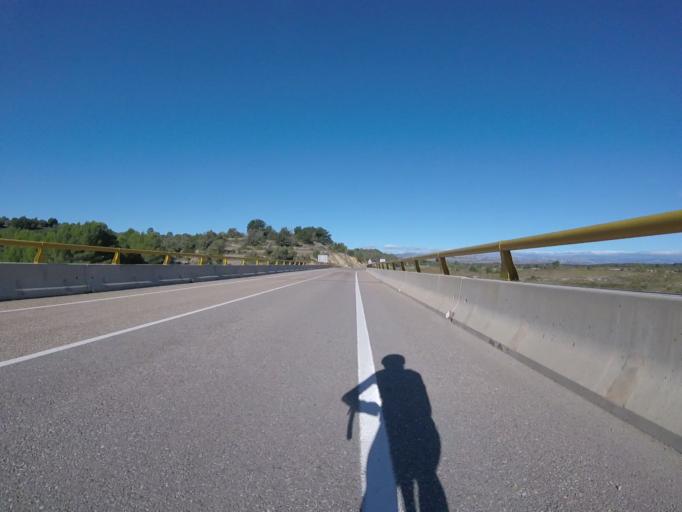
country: ES
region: Valencia
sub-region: Provincia de Castello
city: Cervera del Maestre
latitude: 40.4666
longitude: 0.2491
